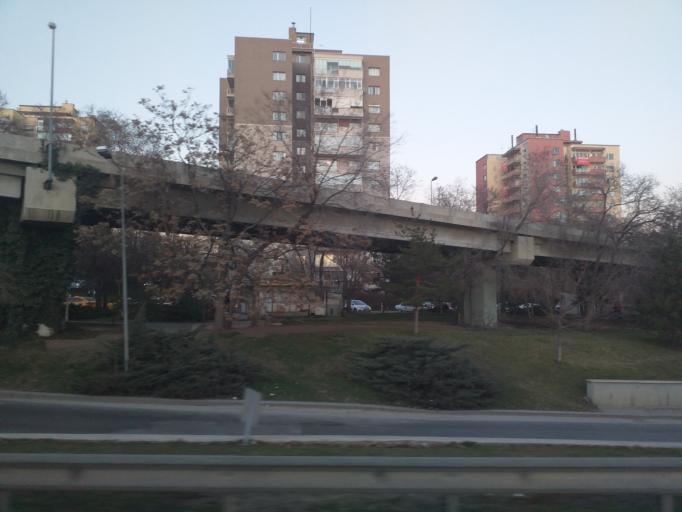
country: TR
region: Ankara
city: Ankara
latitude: 39.9562
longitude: 32.8192
